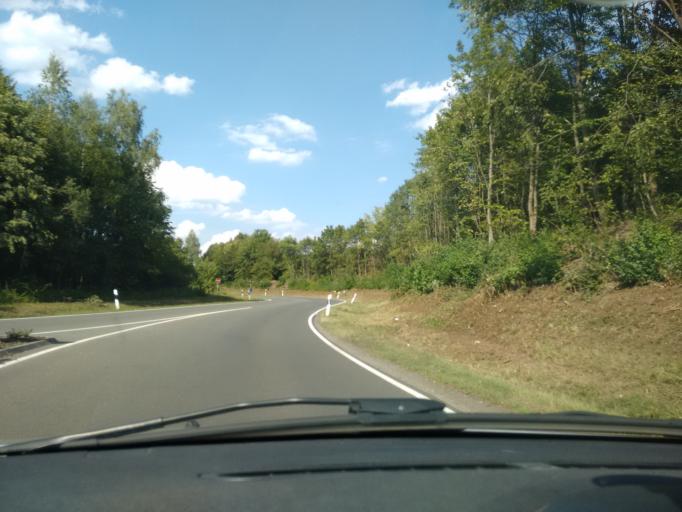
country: DE
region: Rheinland-Pfalz
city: Birkenfeld
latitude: 49.6490
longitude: 7.1757
